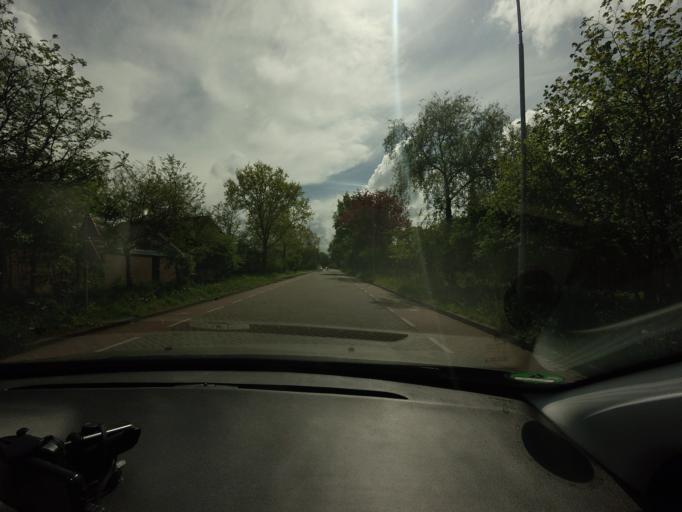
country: NL
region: North Holland
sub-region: Gemeente Beemster
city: Halfweg
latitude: 52.5574
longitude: 4.8434
